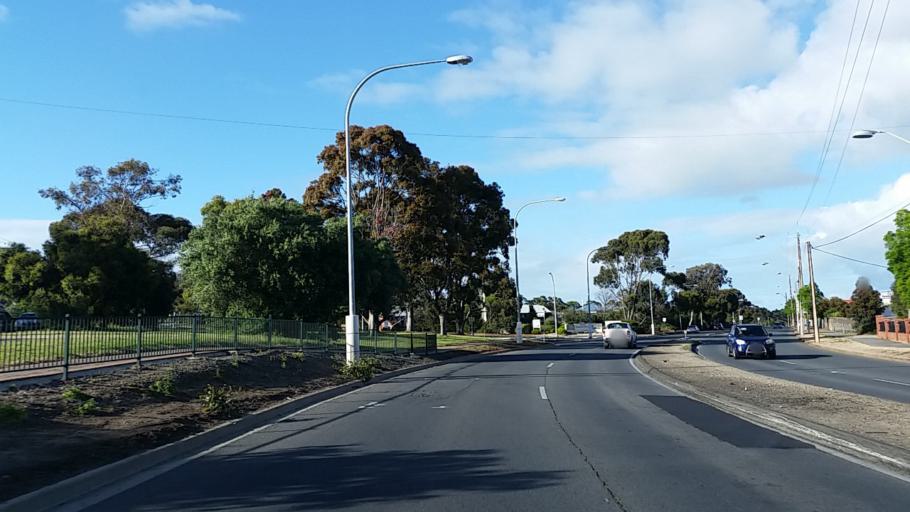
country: AU
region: South Australia
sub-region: Mitcham
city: Clapham
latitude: -34.9992
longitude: 138.5932
